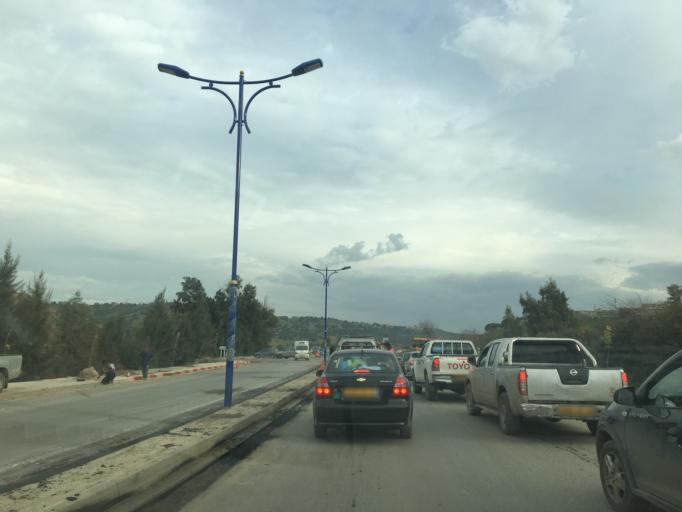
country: DZ
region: Bouira
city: Bouira
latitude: 36.3601
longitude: 3.9007
